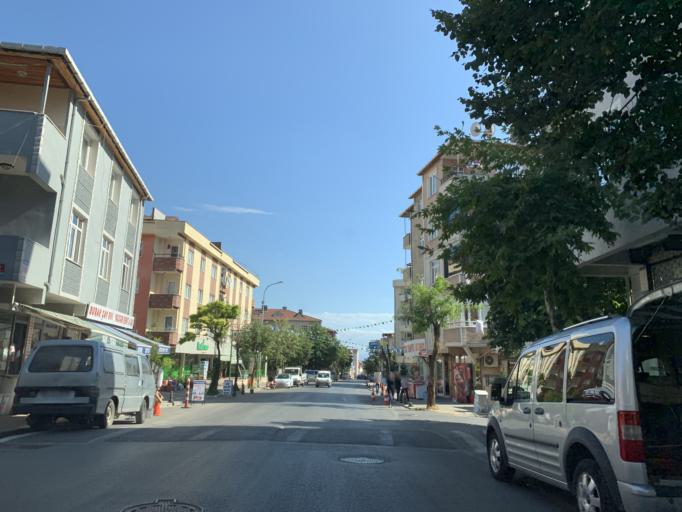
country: TR
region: Istanbul
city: Pendik
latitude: 40.8781
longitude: 29.2809
